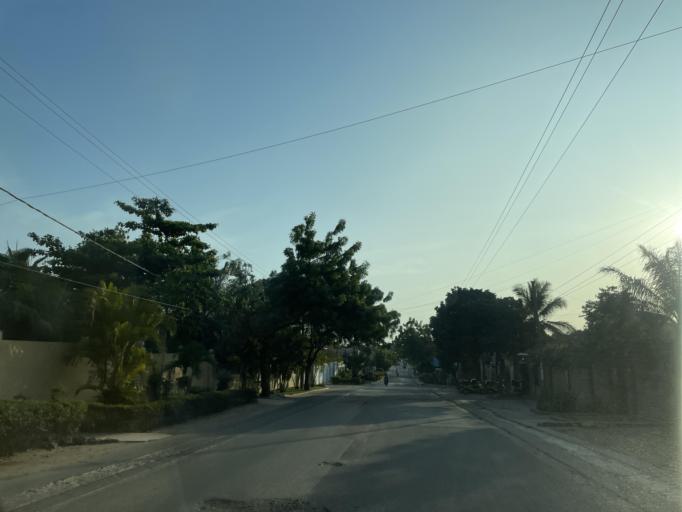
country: AO
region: Luanda
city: Luanda
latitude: -8.9093
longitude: 13.2284
